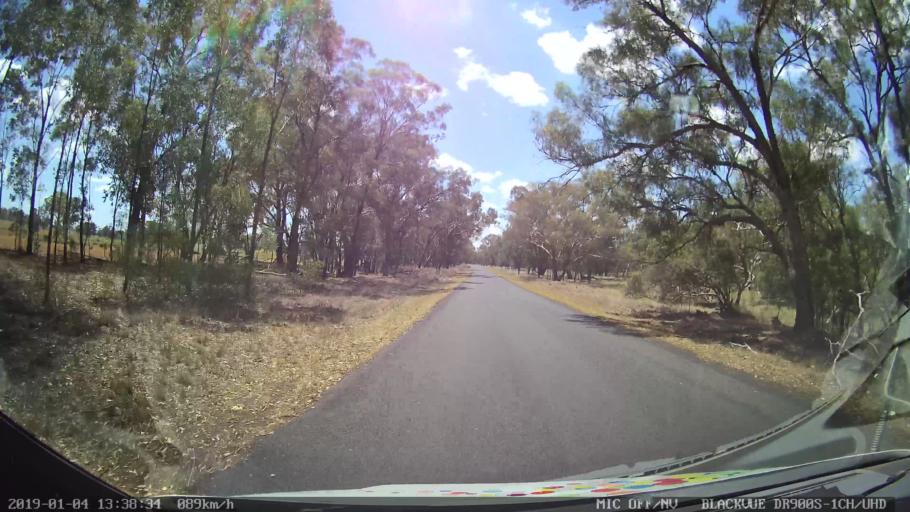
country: AU
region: New South Wales
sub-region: Dubbo Municipality
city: Dubbo
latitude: -32.5365
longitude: 148.5482
